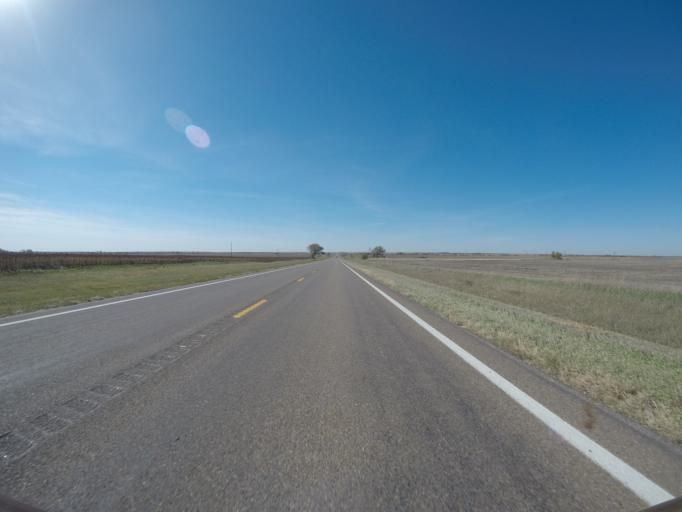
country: US
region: Kansas
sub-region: Smith County
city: Smith Center
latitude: 39.7711
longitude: -98.9565
